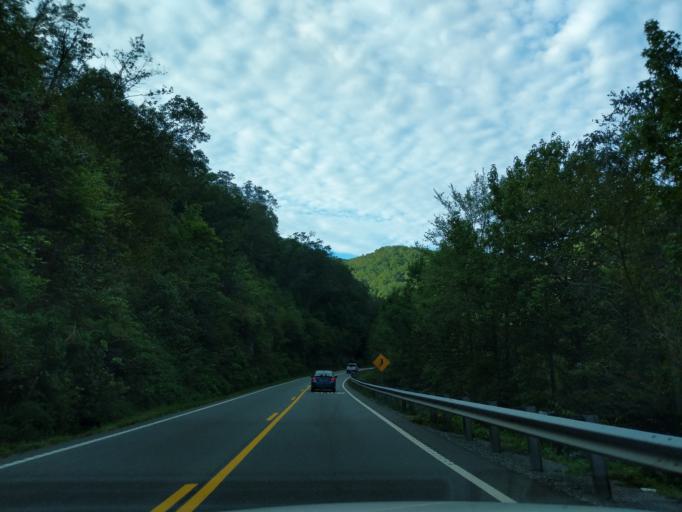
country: US
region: Tennessee
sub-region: Polk County
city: Benton
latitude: 35.0860
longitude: -84.5279
